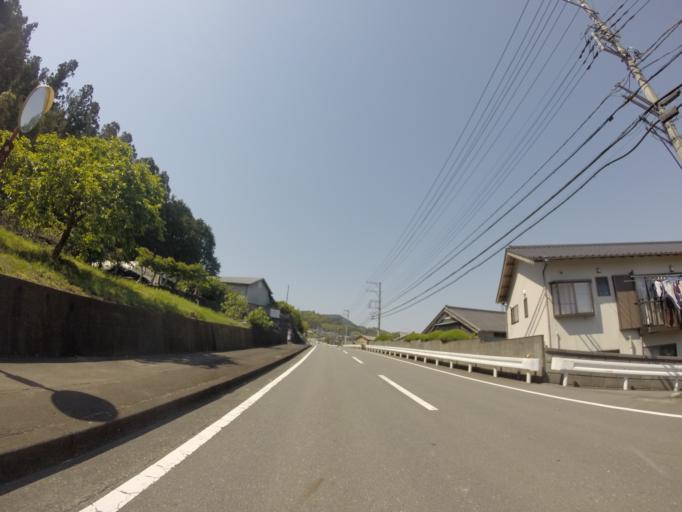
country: JP
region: Shizuoka
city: Fujinomiya
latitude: 35.2073
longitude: 138.5869
